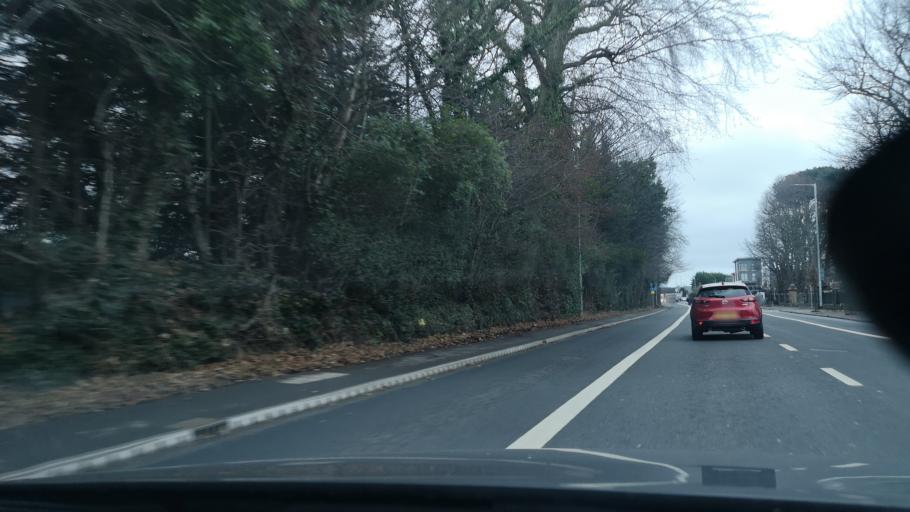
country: GB
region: Northern Ireland
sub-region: Castlereagh District
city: Dundonald
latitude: 54.5942
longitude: -5.8221
